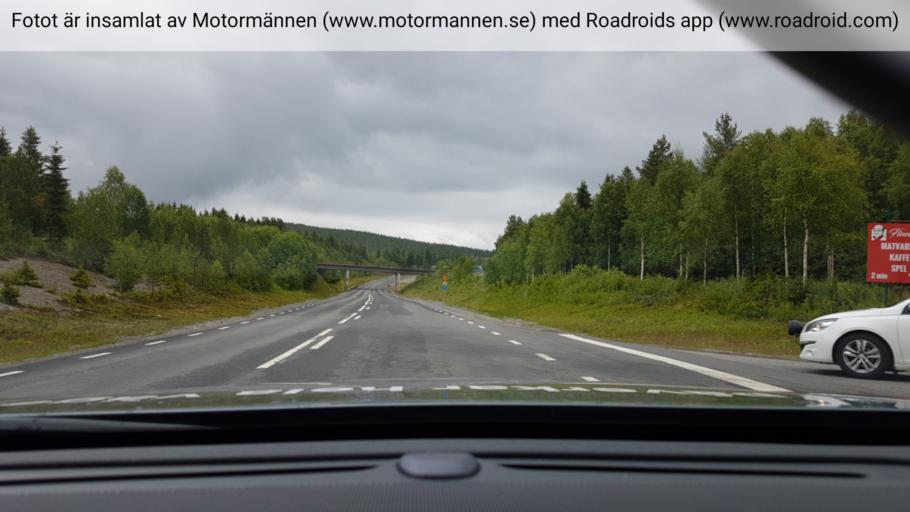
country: SE
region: Vaesterbotten
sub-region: Norsjo Kommun
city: Norsjoe
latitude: 65.2757
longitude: 19.6005
